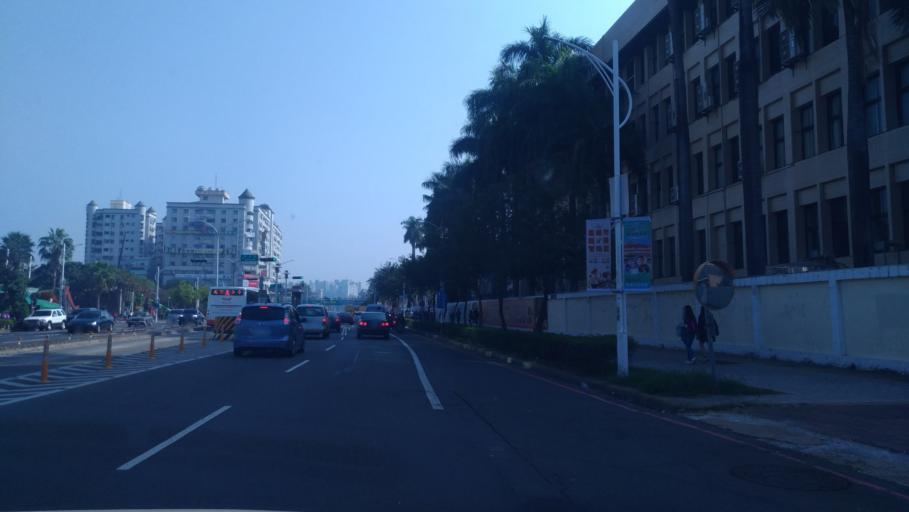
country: TW
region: Taiwan
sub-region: Chiayi
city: Jiayi Shi
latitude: 23.4737
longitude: 120.4494
